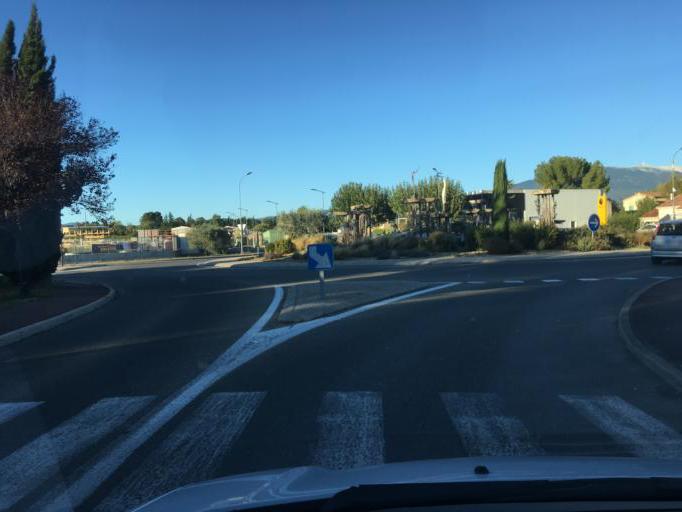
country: FR
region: Provence-Alpes-Cote d'Azur
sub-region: Departement du Vaucluse
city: Mazan
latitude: 44.0577
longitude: 5.1140
